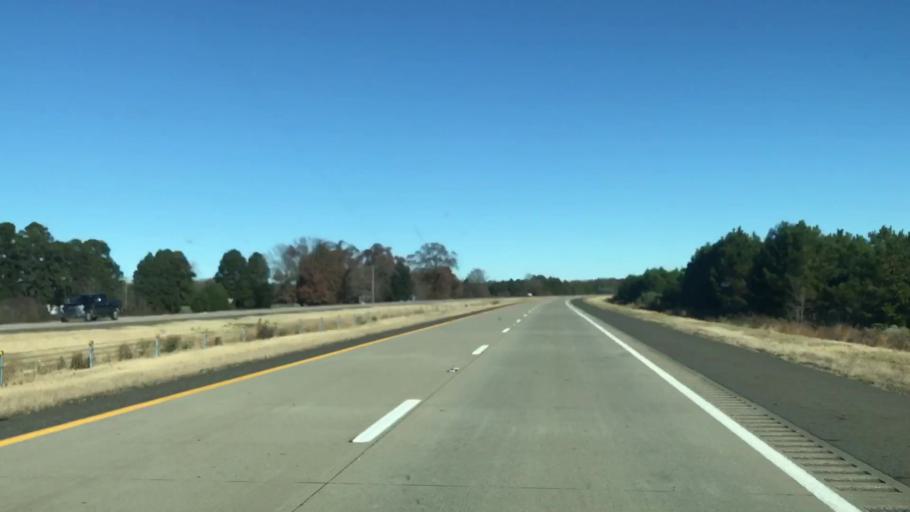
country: US
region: Texas
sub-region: Cass County
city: Queen City
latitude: 33.1967
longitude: -93.8773
